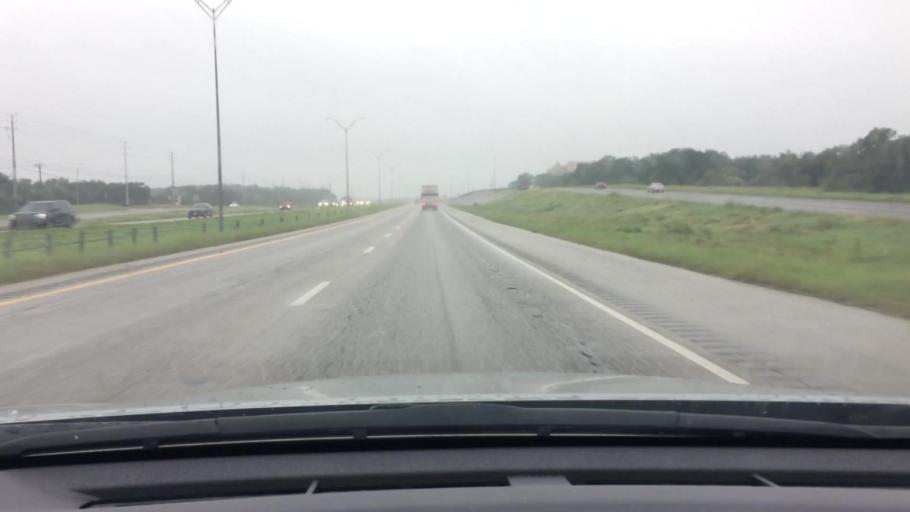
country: US
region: Texas
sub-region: Bexar County
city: Leon Valley
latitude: 29.4687
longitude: -98.6946
